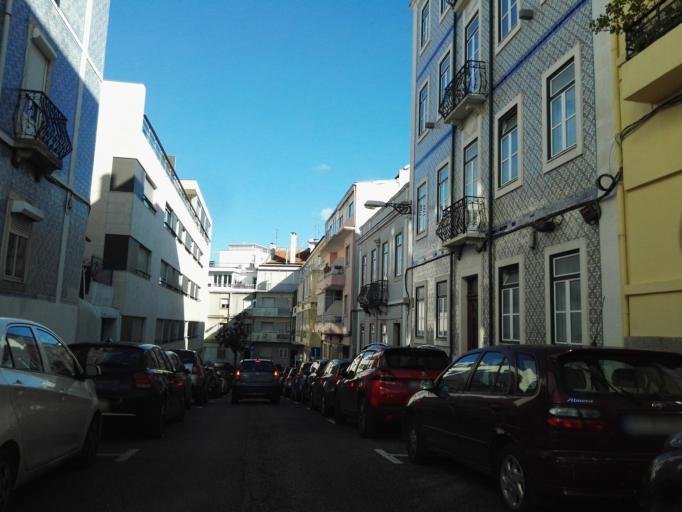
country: PT
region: Setubal
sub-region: Almada
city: Cacilhas
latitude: 38.7112
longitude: -9.1665
